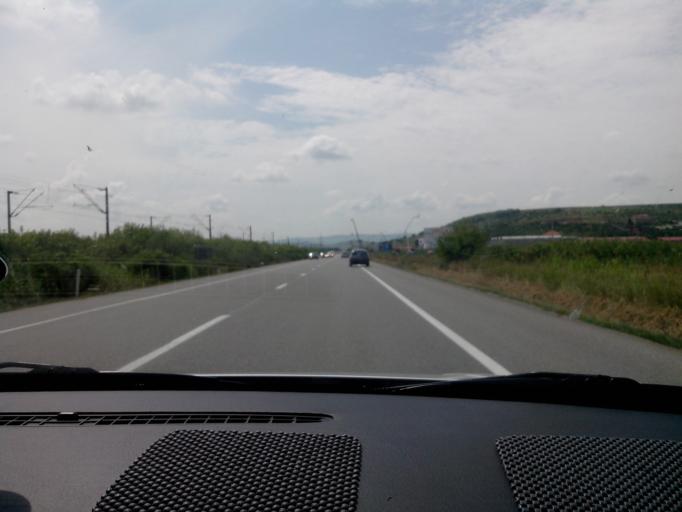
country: RO
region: Cluj
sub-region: Comuna Apahida
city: Apahida
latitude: 46.8328
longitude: 23.7459
